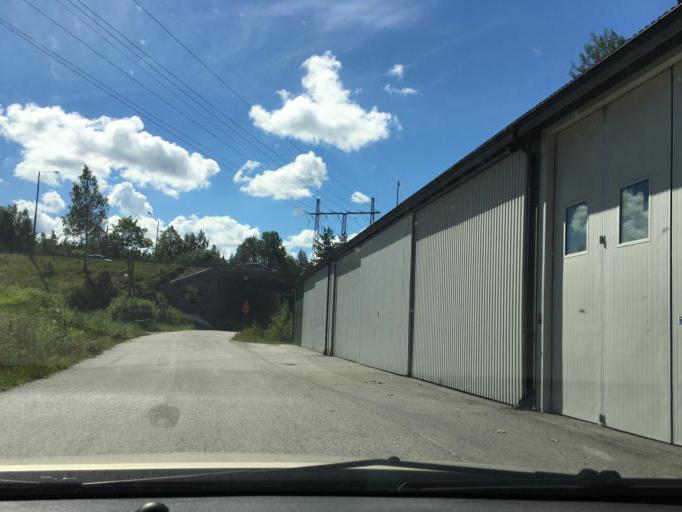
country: SE
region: Stockholm
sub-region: Nacka Kommun
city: Fisksatra
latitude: 59.2931
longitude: 18.2374
